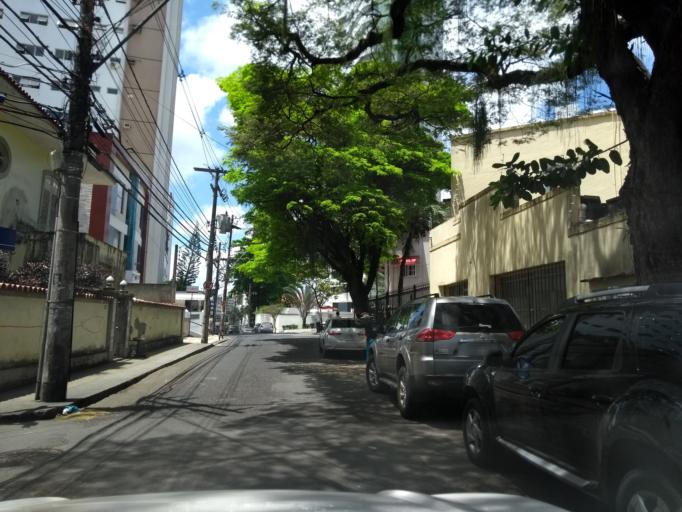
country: BR
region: Bahia
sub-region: Salvador
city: Salvador
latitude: -12.9977
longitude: -38.5223
